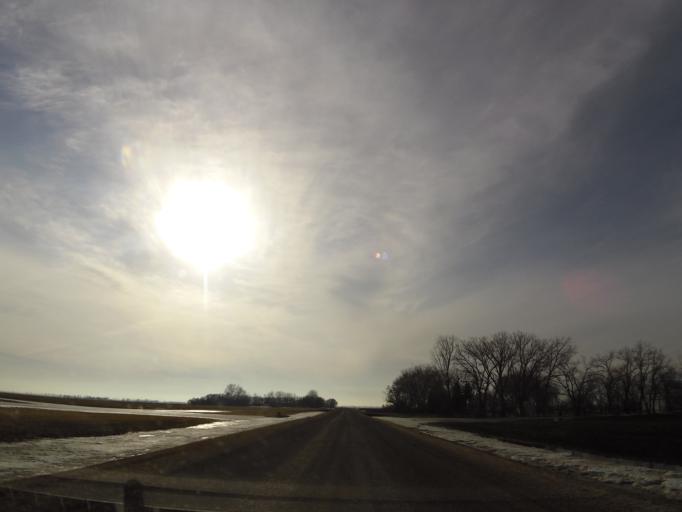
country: US
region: North Dakota
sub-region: Walsh County
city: Grafton
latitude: 48.4265
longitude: -97.2159
